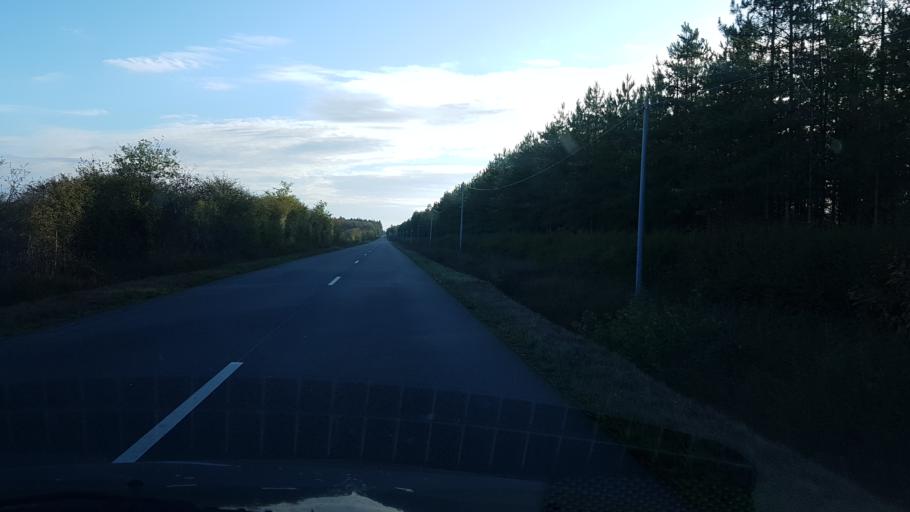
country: FR
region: Centre
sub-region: Departement du Cher
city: Brinon-sur-Sauldre
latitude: 47.6631
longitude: 2.2271
